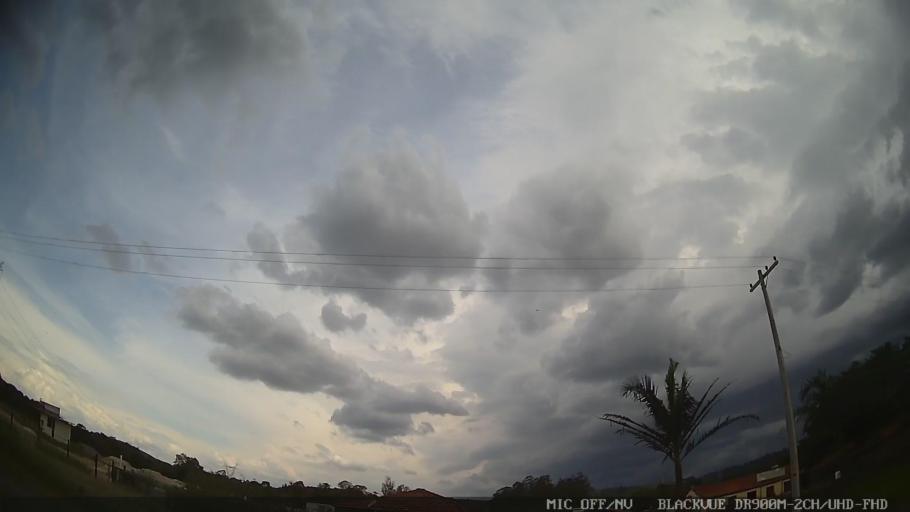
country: BR
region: Sao Paulo
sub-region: Amparo
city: Amparo
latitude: -22.8485
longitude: -46.7806
